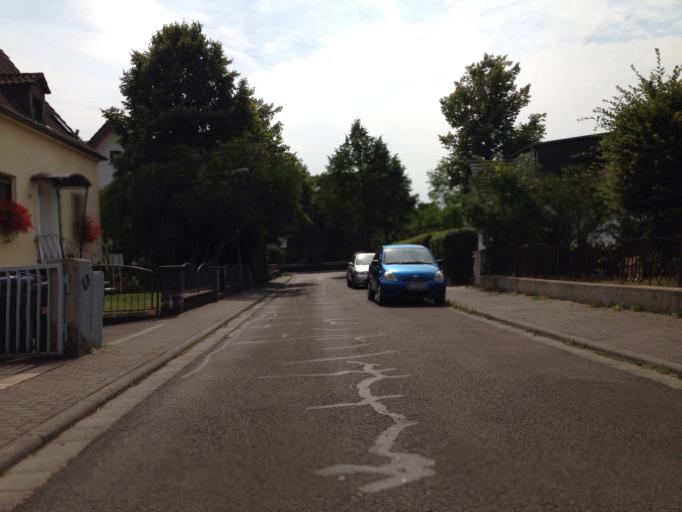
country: DE
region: Hesse
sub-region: Regierungsbezirk Giessen
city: Giessen
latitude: 50.5786
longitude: 8.6956
